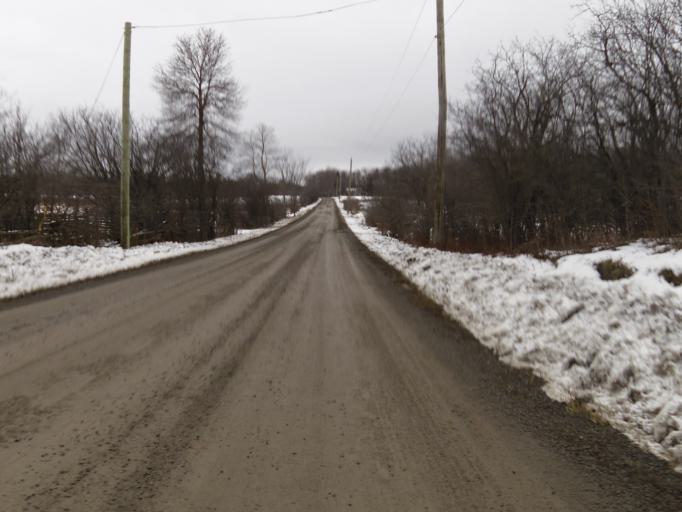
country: CA
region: Ontario
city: Carleton Place
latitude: 45.1972
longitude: -76.2149
